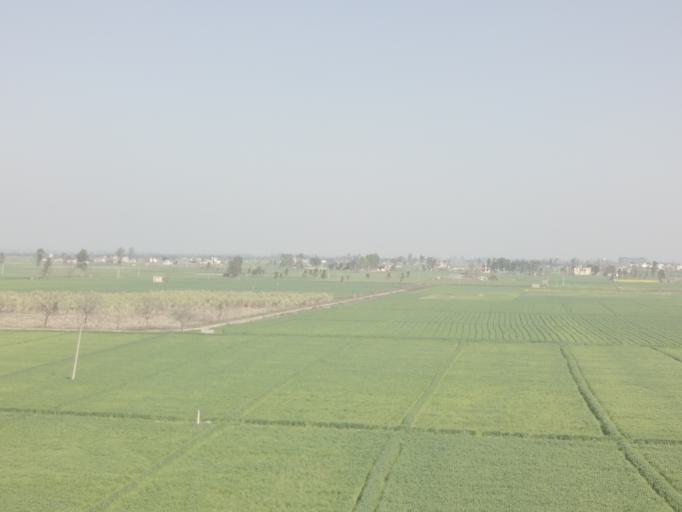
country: IN
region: Punjab
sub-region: Shahid Bhagat Singh Nagar
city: Rahon
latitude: 31.0243
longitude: 76.0931
